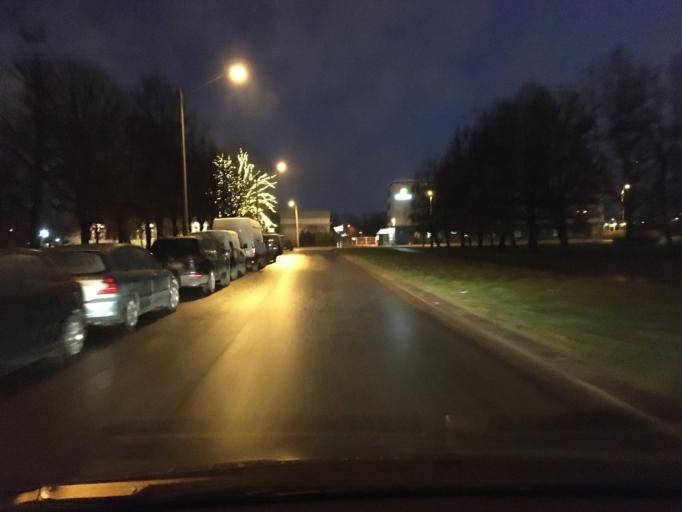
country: EE
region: Harju
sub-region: Tallinna linn
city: Kose
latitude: 59.4352
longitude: 24.8328
